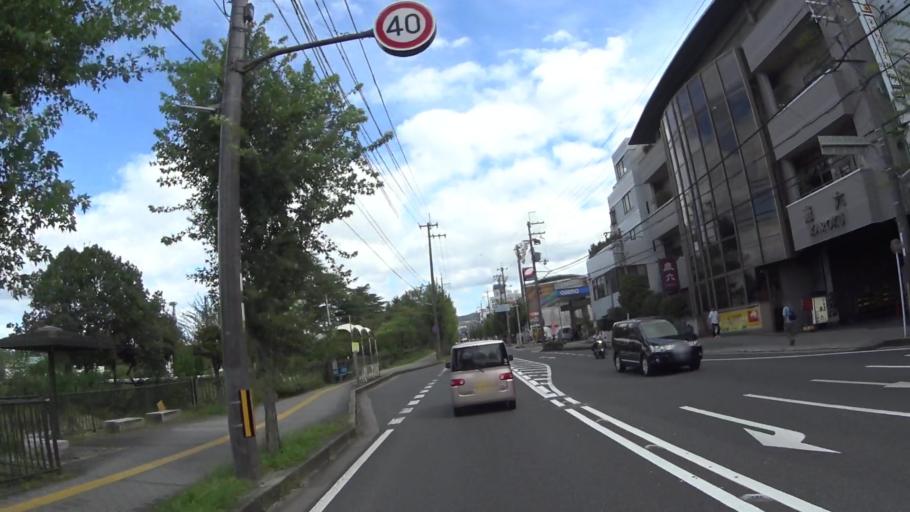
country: JP
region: Kyoto
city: Uji
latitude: 34.8741
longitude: 135.7706
